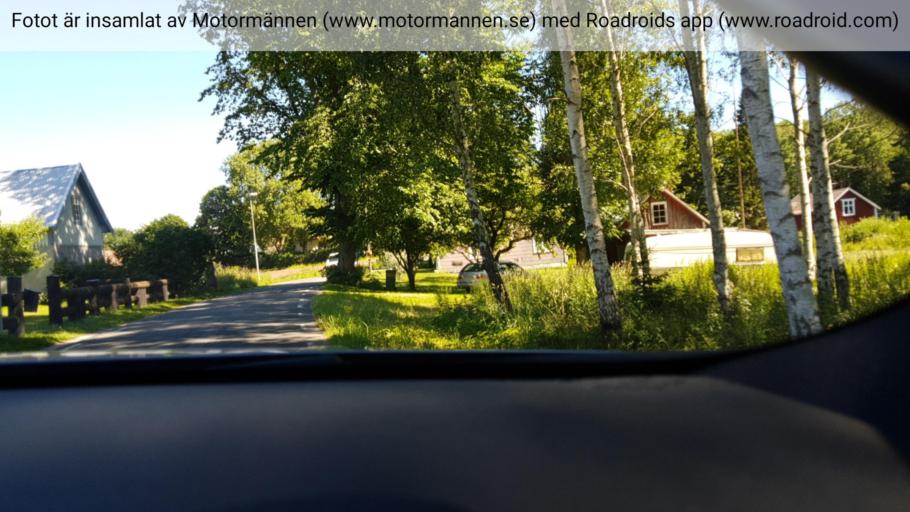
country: SE
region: Vaestra Goetaland
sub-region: Falkopings Kommun
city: Falkoeping
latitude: 58.0704
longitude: 13.5274
